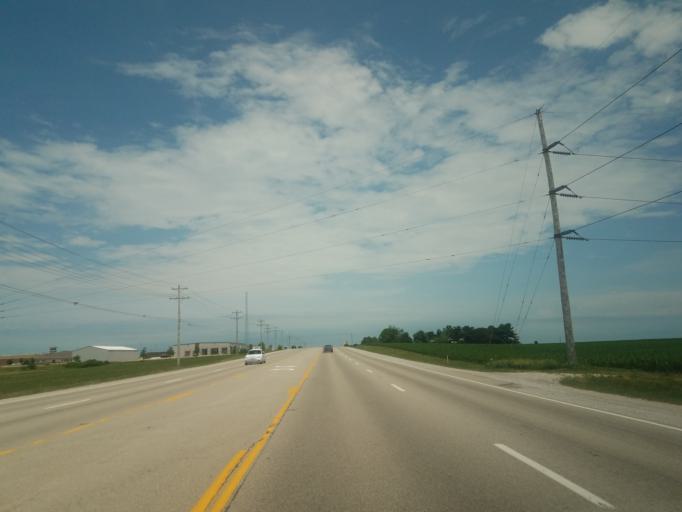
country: US
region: Illinois
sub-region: McLean County
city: Downs
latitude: 40.4653
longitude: -88.9020
